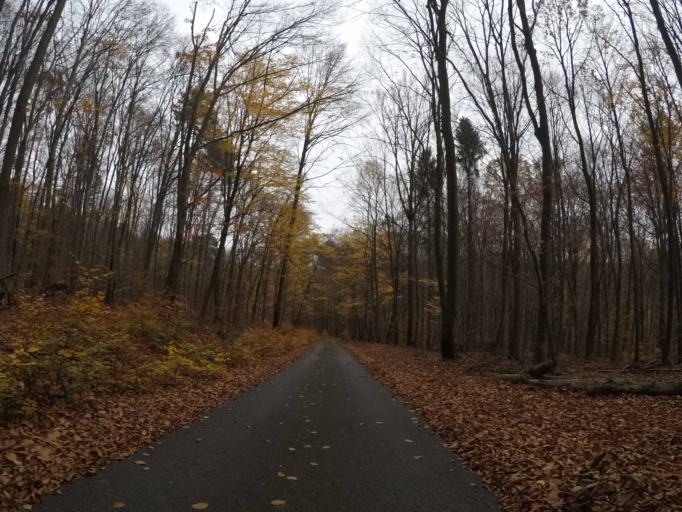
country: SK
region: Presovsky
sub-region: Okres Presov
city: Presov
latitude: 48.8845
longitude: 21.1963
